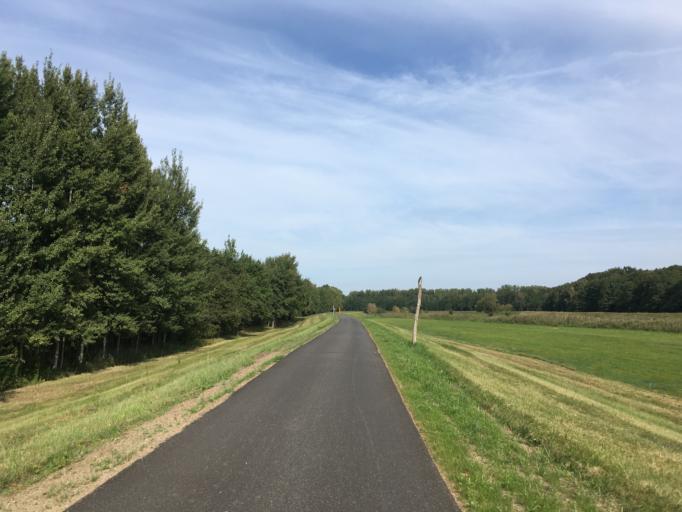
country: DE
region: Brandenburg
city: Forst
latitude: 51.8124
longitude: 14.5995
